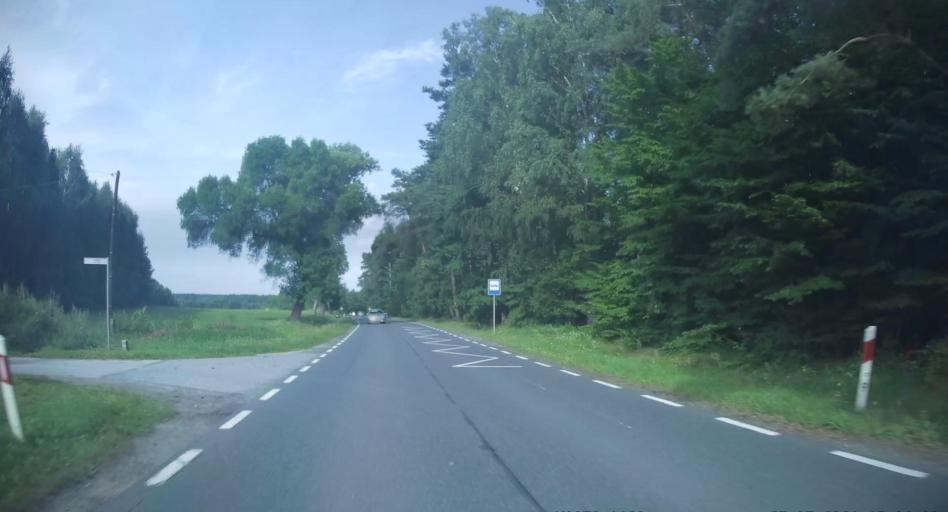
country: PL
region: Lodz Voivodeship
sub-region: Powiat tomaszowski
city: Inowlodz
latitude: 51.5500
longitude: 20.2454
